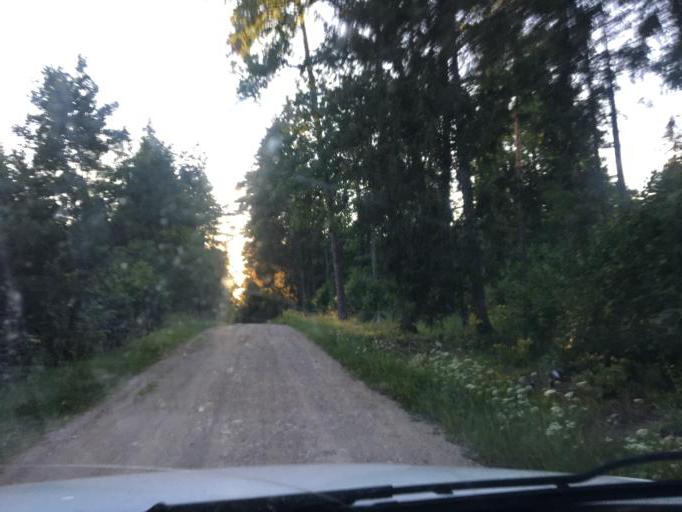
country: LV
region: Kuldigas Rajons
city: Kuldiga
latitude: 56.9809
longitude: 22.0263
